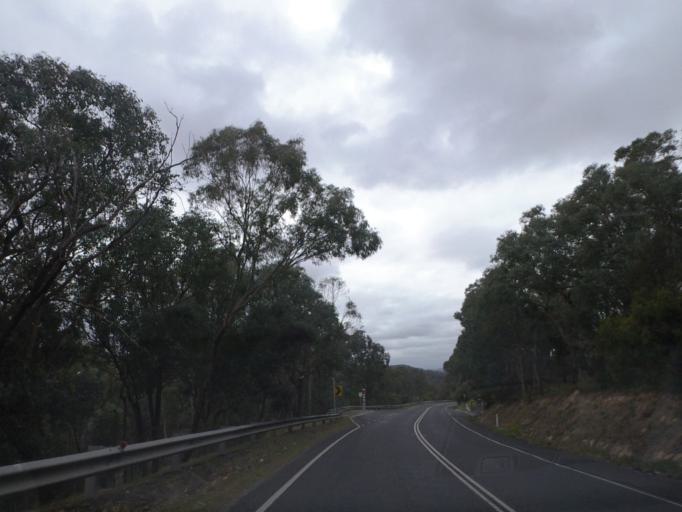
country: AU
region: Victoria
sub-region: Nillumbik
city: North Warrandyte
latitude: -37.7460
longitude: 145.2005
